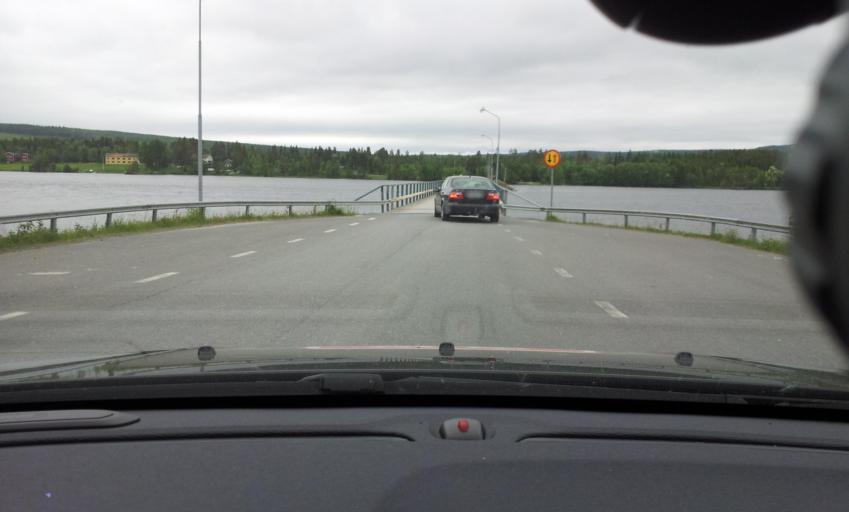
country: SE
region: Jaemtland
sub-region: Are Kommun
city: Jarpen
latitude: 63.3080
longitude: 13.6501
